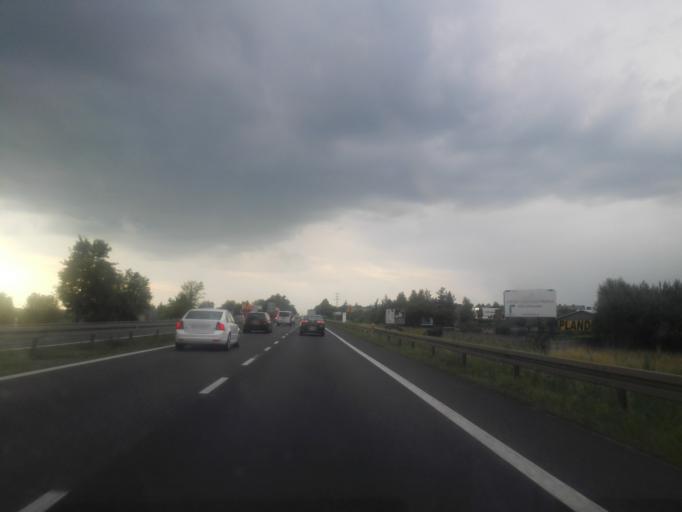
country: PL
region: Silesian Voivodeship
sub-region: Powiat czestochowski
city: Huta Stara B
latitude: 50.7360
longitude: 19.1608
